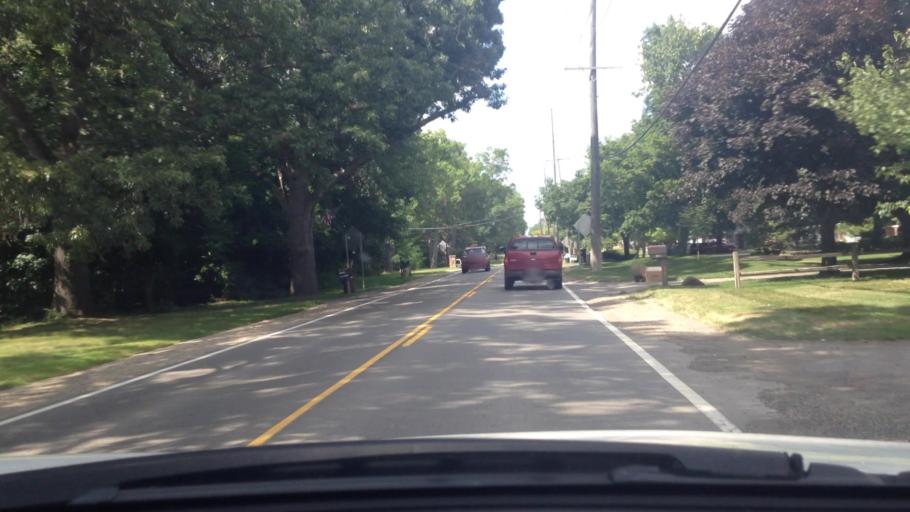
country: US
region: Michigan
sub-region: Oakland County
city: Waterford
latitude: 42.6913
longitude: -83.3483
